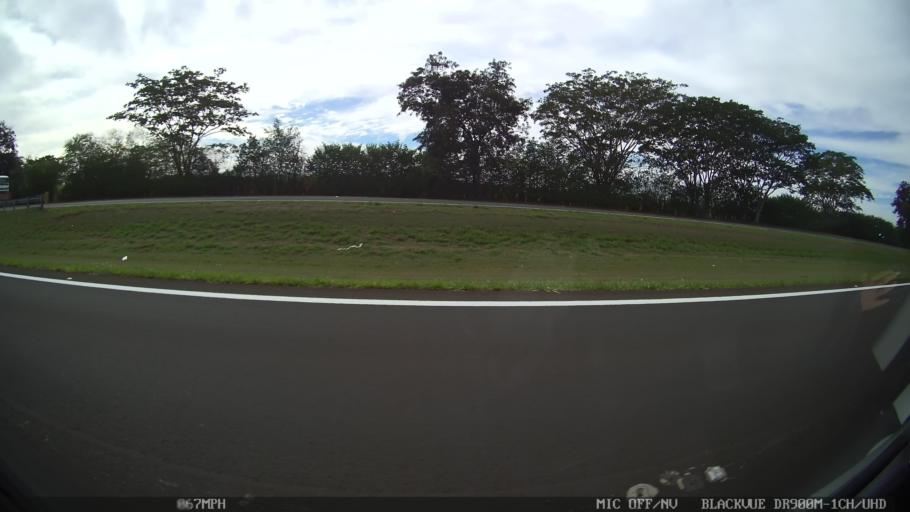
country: BR
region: Sao Paulo
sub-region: Taquaritinga
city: Taquaritinga
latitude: -21.4708
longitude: -48.6057
